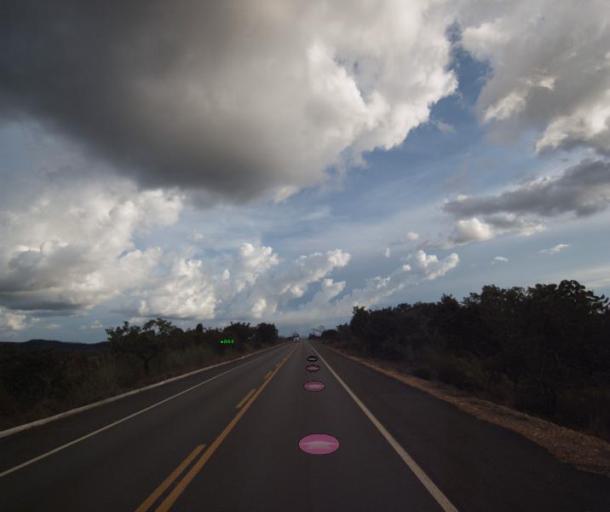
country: BR
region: Goias
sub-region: Niquelandia
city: Niquelandia
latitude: -14.7054
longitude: -48.6038
